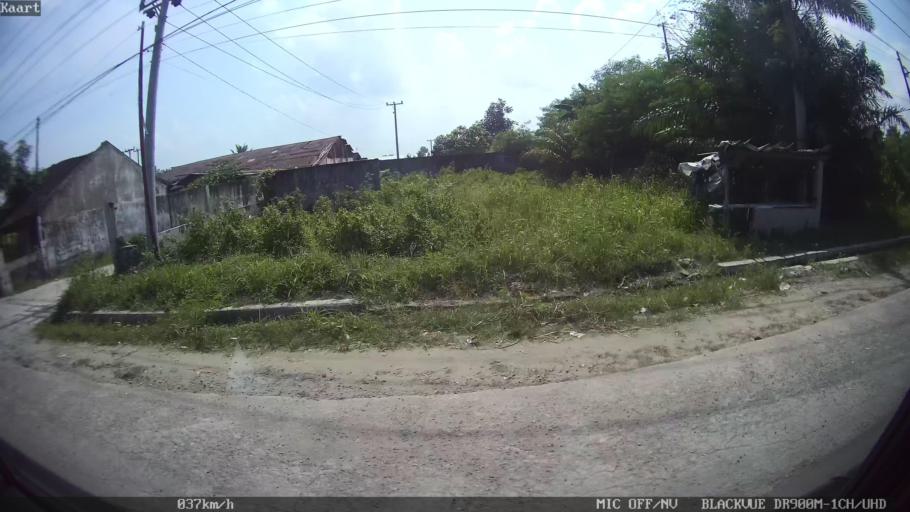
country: ID
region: Lampung
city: Natar
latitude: -5.2756
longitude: 105.1876
